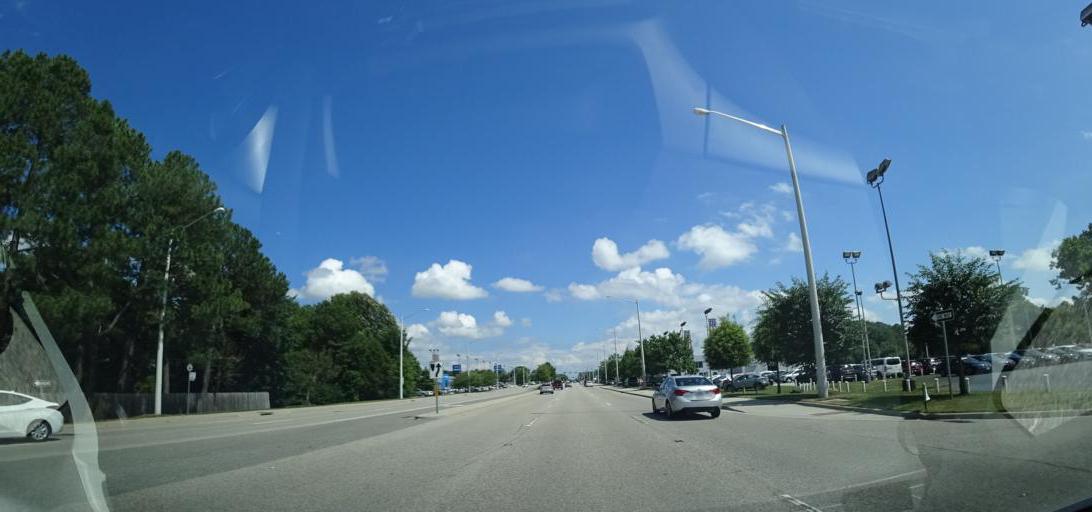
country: US
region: Virginia
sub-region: York County
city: Yorktown
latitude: 37.1532
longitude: -76.5315
